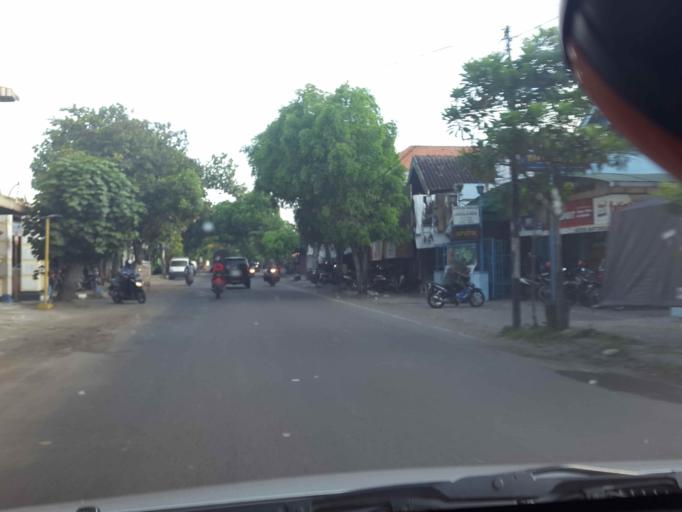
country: ID
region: Central Java
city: Sragen
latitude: -7.4237
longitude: 111.0323
